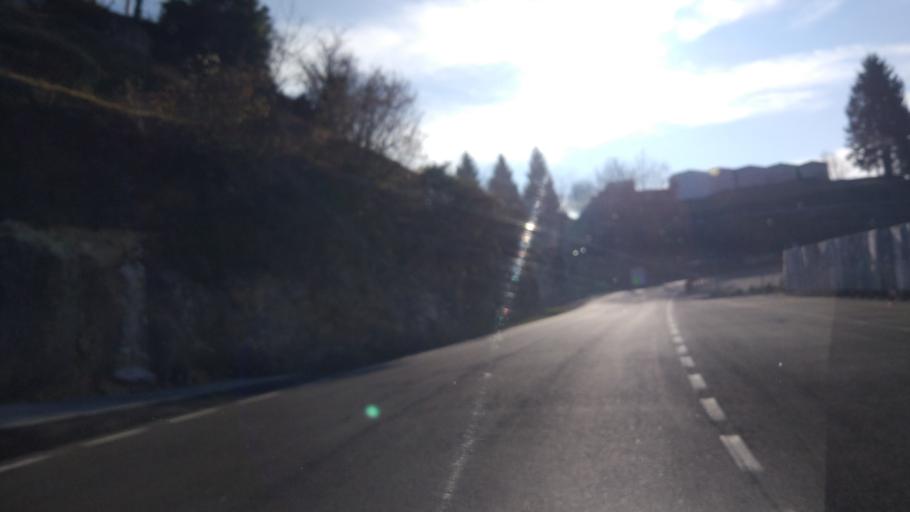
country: IT
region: Veneto
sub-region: Provincia di Verona
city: Selva di Progno
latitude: 45.6094
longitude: 11.1794
